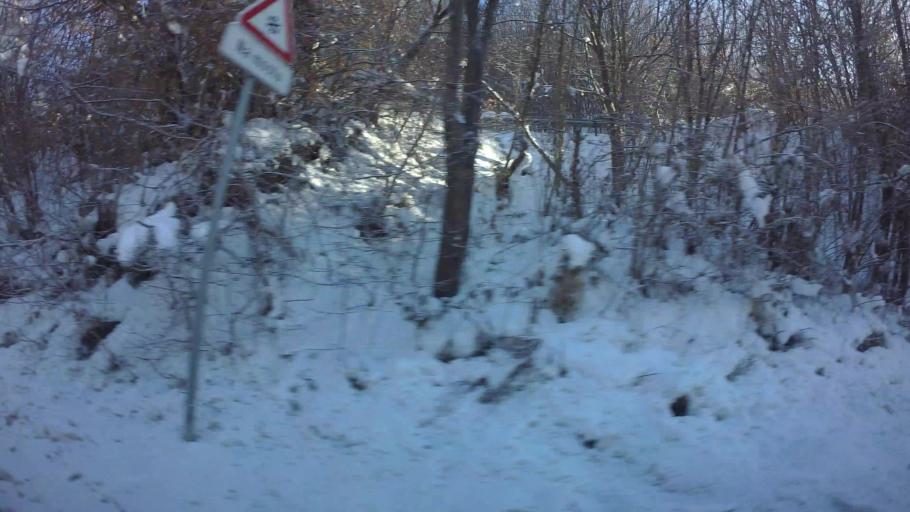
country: BA
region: Federation of Bosnia and Herzegovina
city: Kobilja Glava
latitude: 43.8901
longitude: 18.4170
